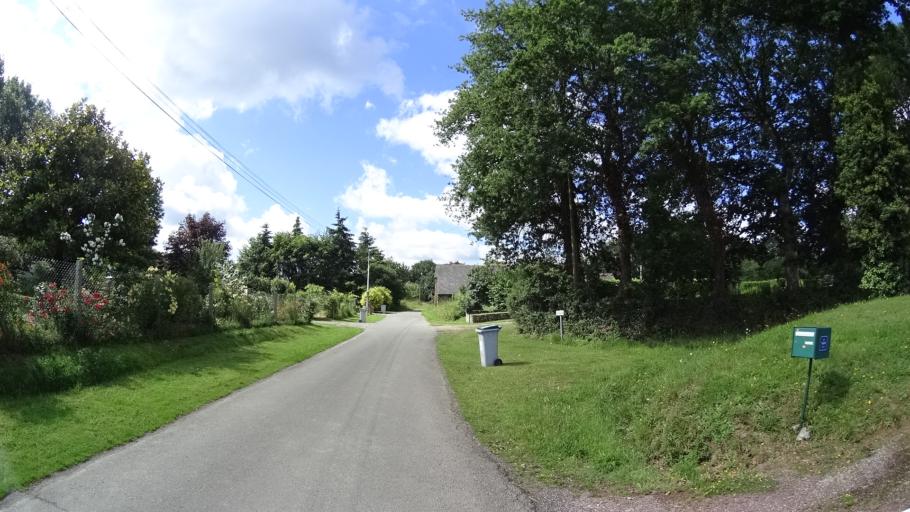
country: FR
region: Brittany
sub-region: Departement d'Ille-et-Vilaine
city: Le Rheu
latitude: 48.1131
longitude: -1.8014
